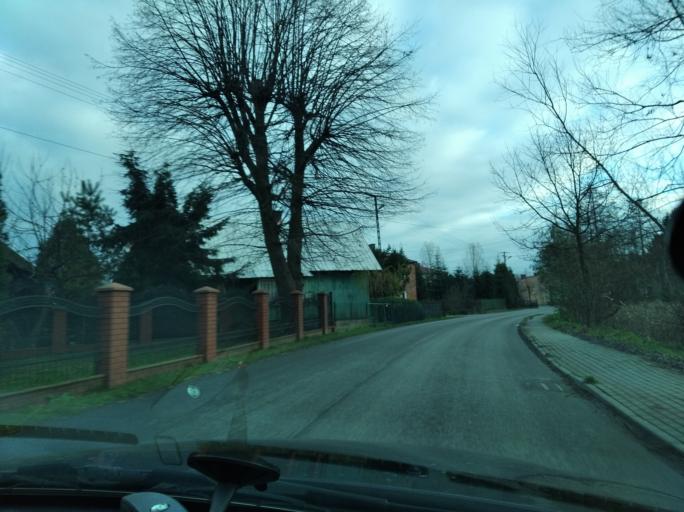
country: PL
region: Subcarpathian Voivodeship
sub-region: Powiat rzeszowski
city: Krasne
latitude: 50.0709
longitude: 22.1149
